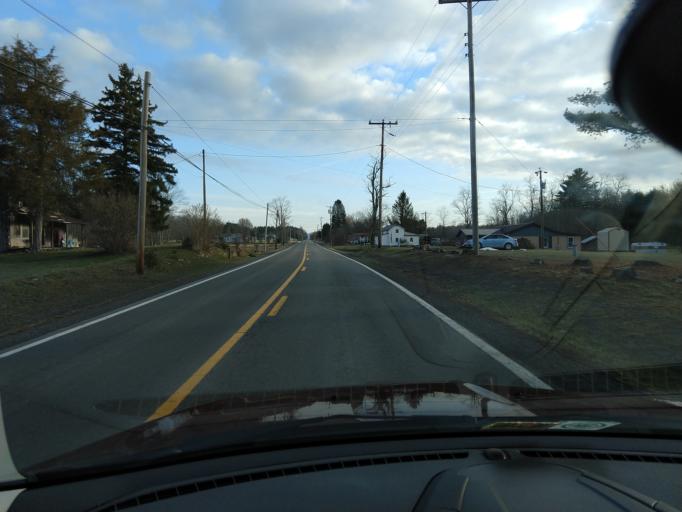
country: US
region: West Virginia
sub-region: Pocahontas County
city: Marlinton
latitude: 38.0765
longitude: -80.2852
